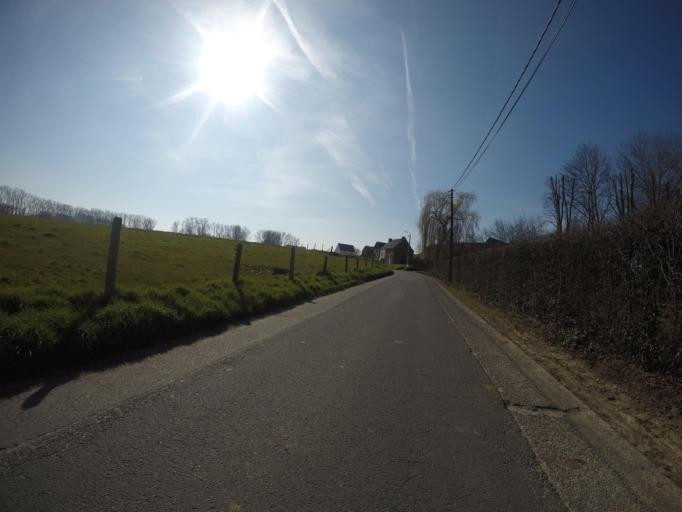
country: BE
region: Flanders
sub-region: Provincie Oost-Vlaanderen
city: Geraardsbergen
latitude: 50.7910
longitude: 3.8614
